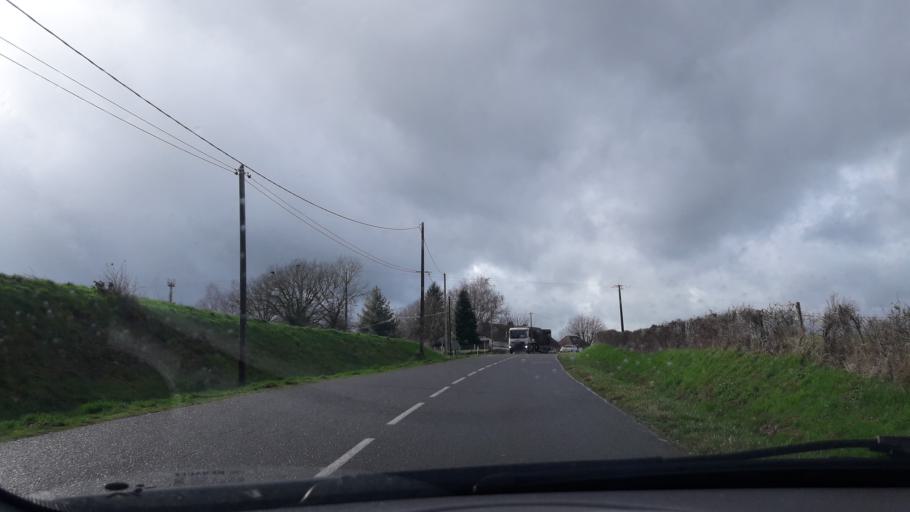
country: FR
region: Limousin
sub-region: Departement de la Haute-Vienne
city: Pierre-Buffiere
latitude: 45.7118
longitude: 1.3629
